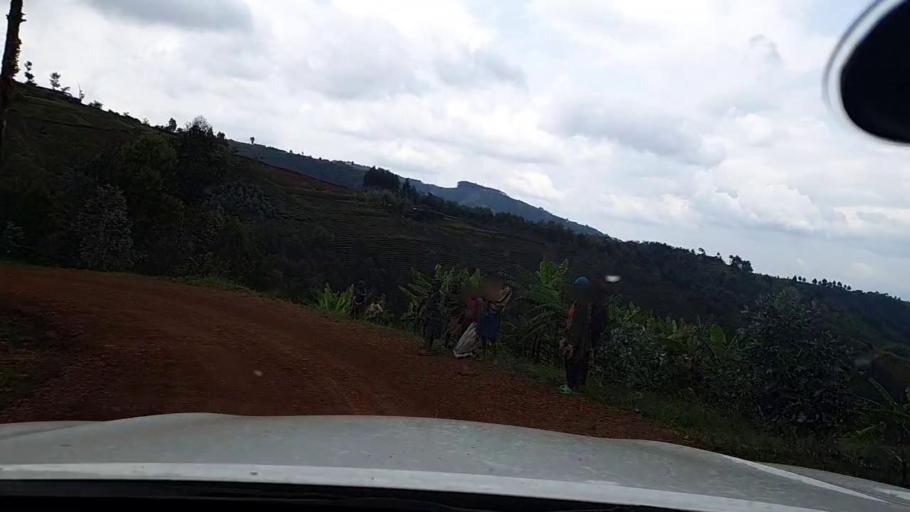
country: RW
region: Western Province
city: Kibuye
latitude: -2.1706
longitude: 29.4365
